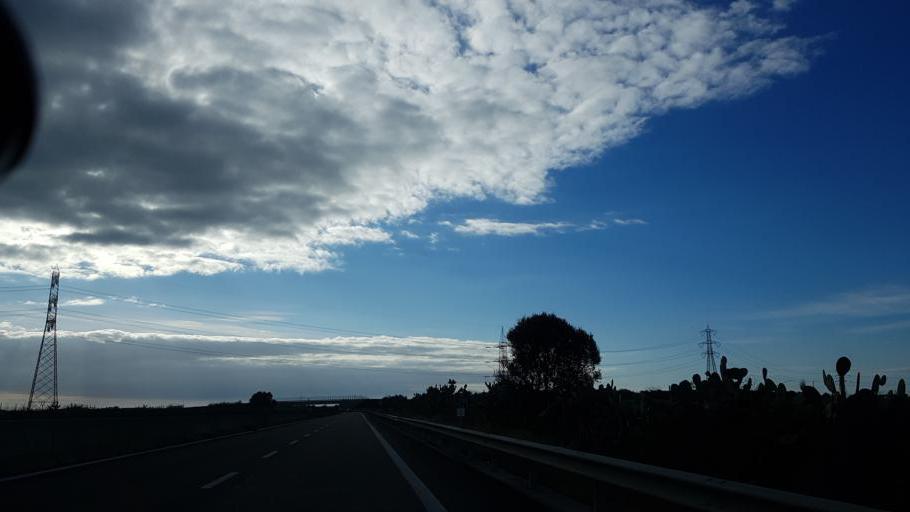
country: IT
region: Apulia
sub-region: Provincia di Brindisi
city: La Rosa
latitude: 40.6041
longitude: 17.9648
